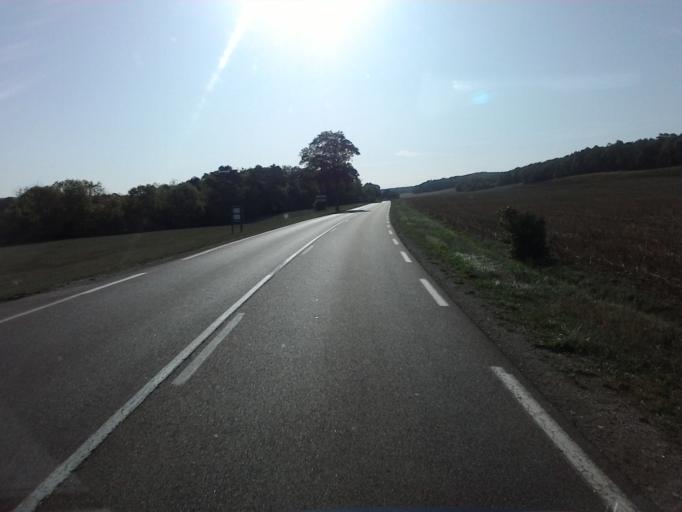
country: FR
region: Champagne-Ardenne
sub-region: Departement de l'Aube
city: Bar-sur-Seine
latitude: 48.1329
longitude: 4.3341
